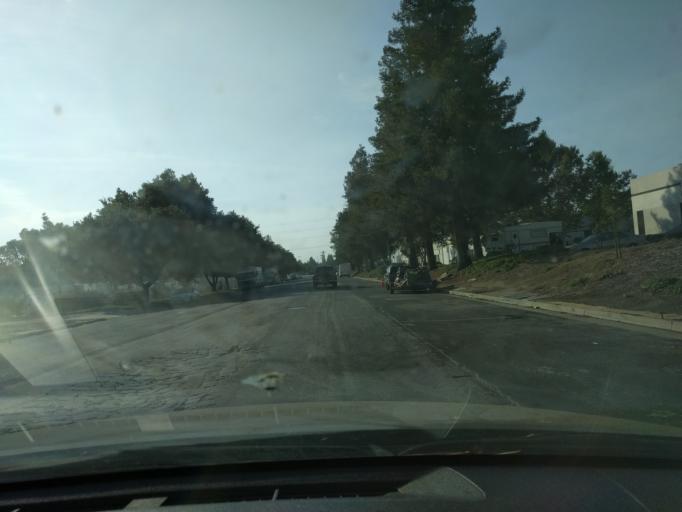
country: US
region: California
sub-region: Santa Clara County
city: Milpitas
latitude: 37.3934
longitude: -121.9143
